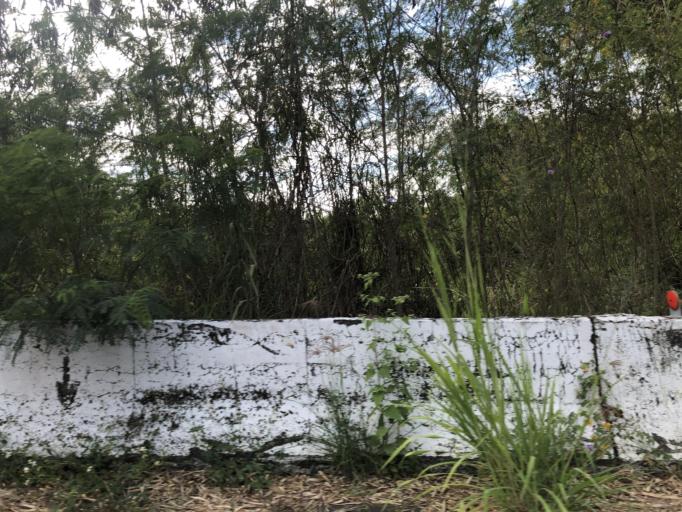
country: TW
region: Taiwan
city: Yujing
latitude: 23.0157
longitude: 120.4167
